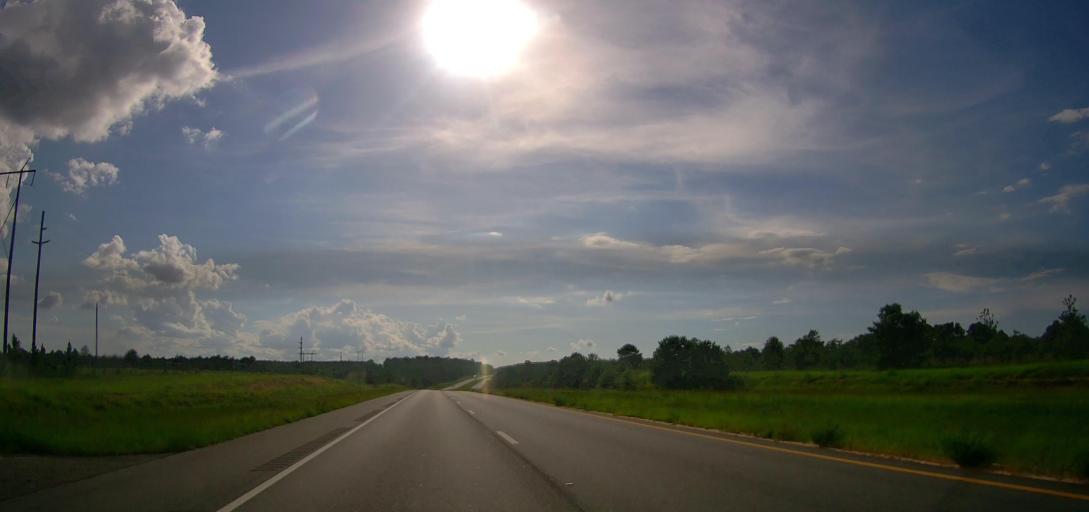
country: US
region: Georgia
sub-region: Taylor County
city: Butler
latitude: 32.5925
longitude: -84.3900
